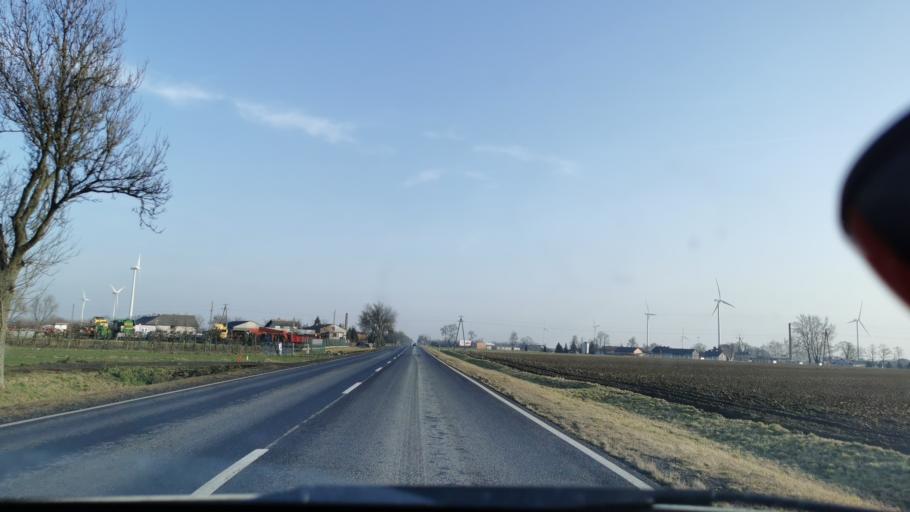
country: PL
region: Lodz Voivodeship
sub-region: Powiat sieradzki
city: Blaszki
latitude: 51.6685
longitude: 18.3791
